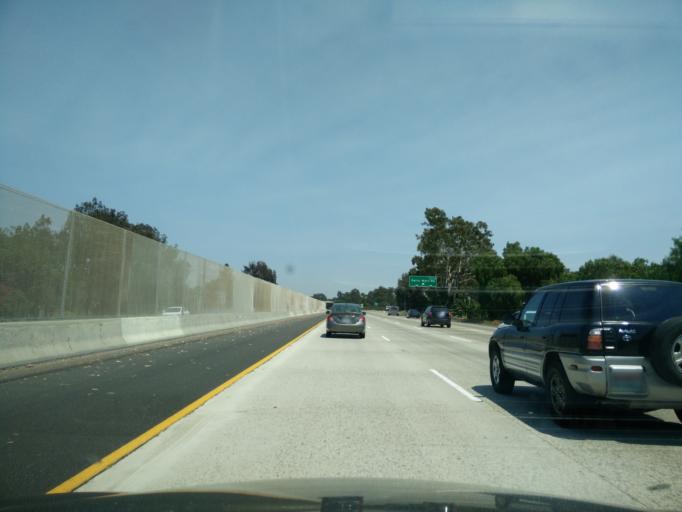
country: US
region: California
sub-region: San Diego County
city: Imperial Beach
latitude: 32.5609
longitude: -117.0667
